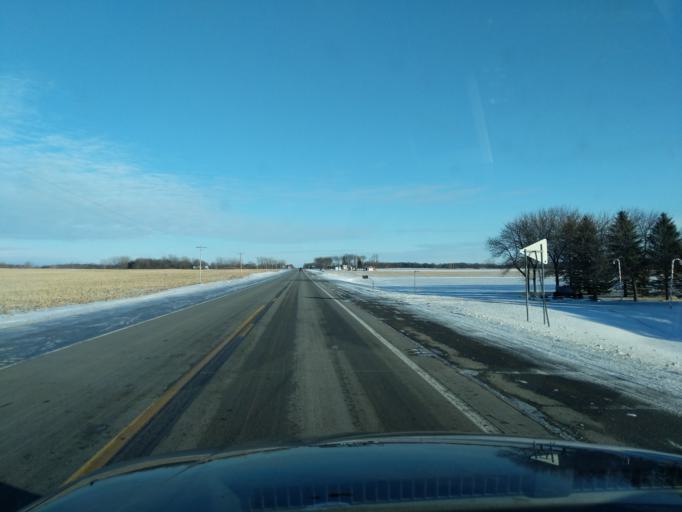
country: US
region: Minnesota
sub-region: McLeod County
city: Hutchinson
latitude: 44.8929
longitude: -94.3132
